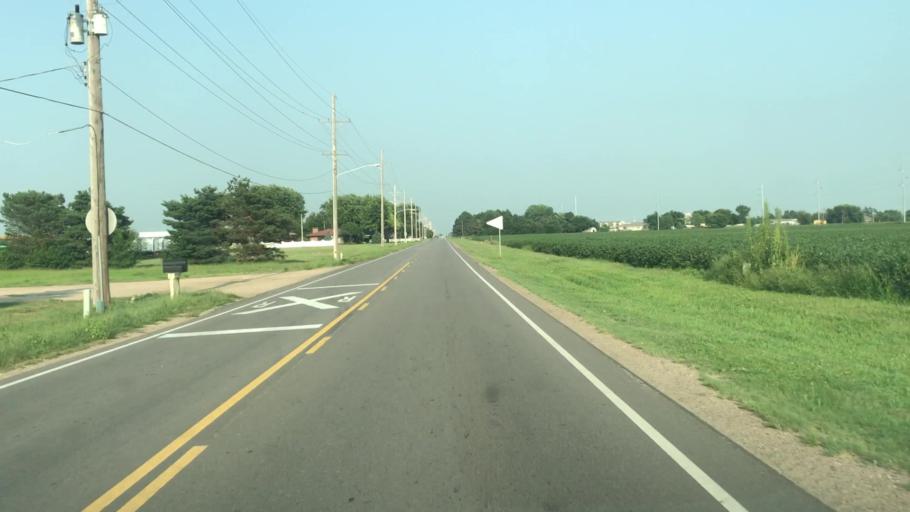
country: US
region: Nebraska
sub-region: Hall County
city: Grand Island
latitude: 40.9456
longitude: -98.3316
